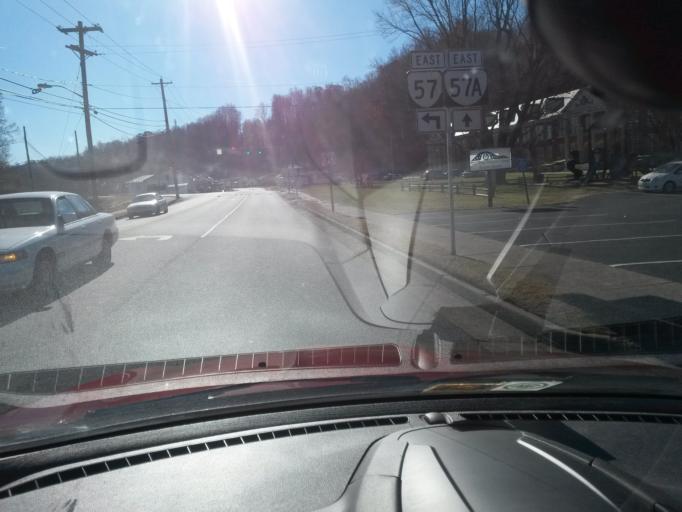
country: US
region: Virginia
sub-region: Henry County
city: Bassett
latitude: 36.7633
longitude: -79.9960
